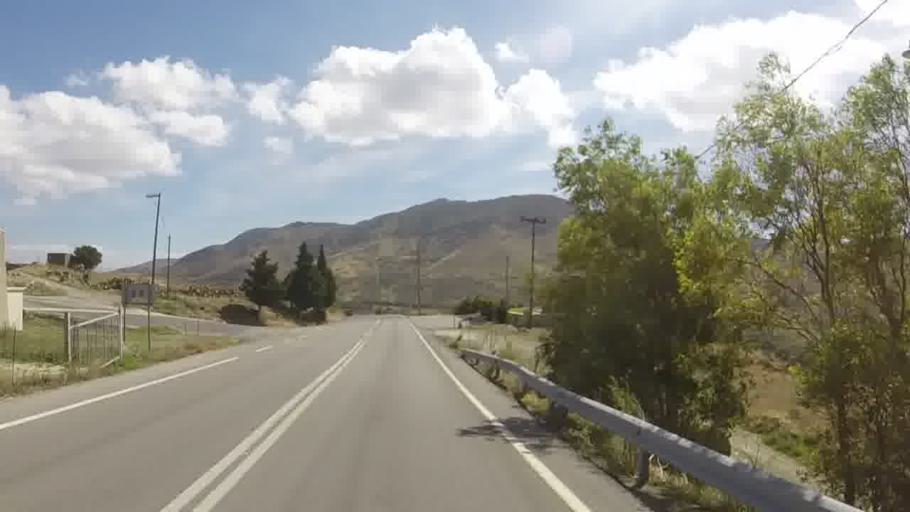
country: GR
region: Crete
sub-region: Nomos Rethymnis
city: Agia Galini
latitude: 35.1496
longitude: 24.6275
